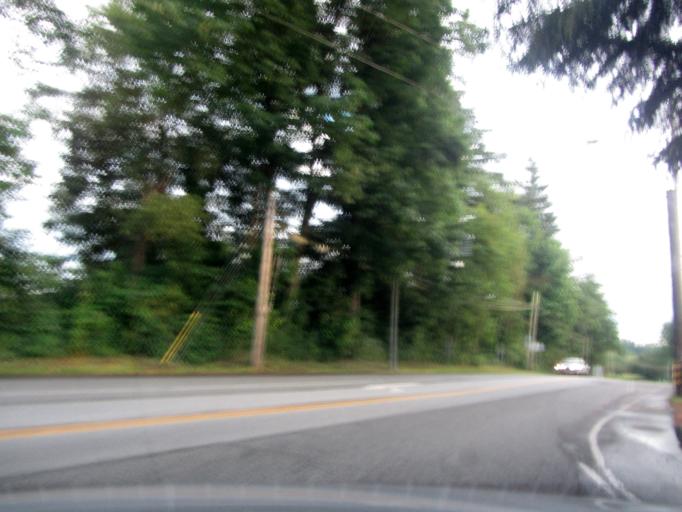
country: CA
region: British Columbia
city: Walnut Grove
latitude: 49.1625
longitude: -122.5862
